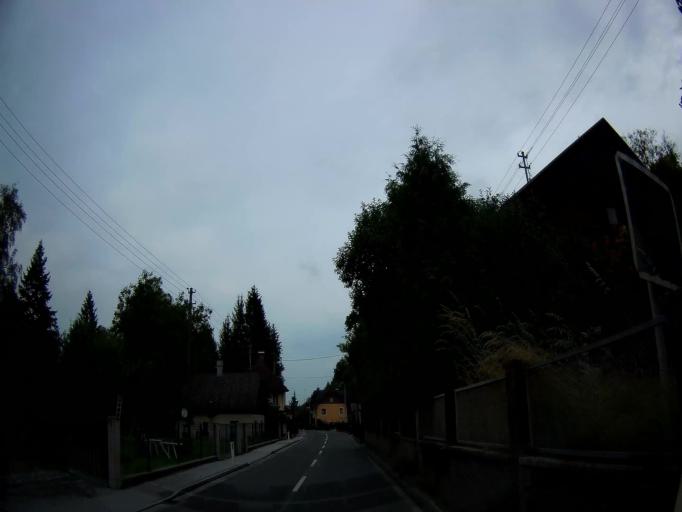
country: AT
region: Salzburg
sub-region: Politischer Bezirk Salzburg-Umgebung
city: Mattsee
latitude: 48.0961
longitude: 13.1499
